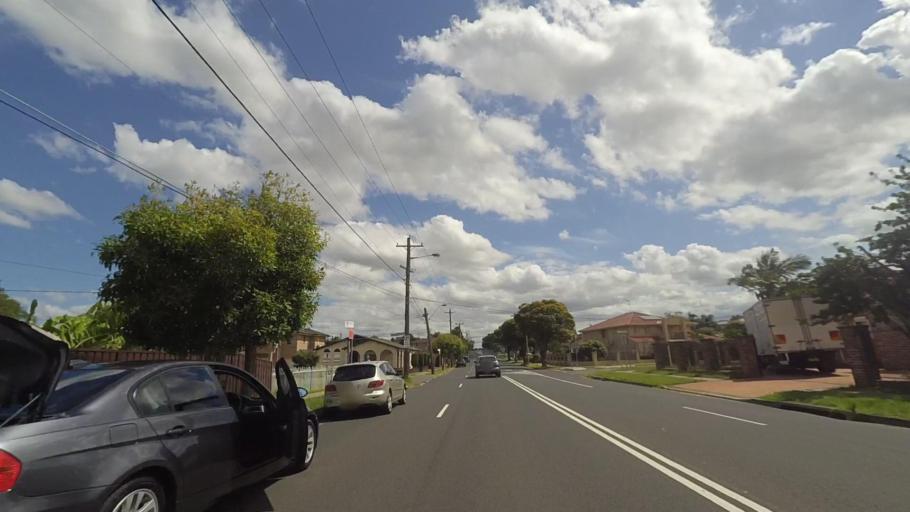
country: AU
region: New South Wales
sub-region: Fairfield
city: Fairfield Heights
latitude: -33.8644
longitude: 150.9507
